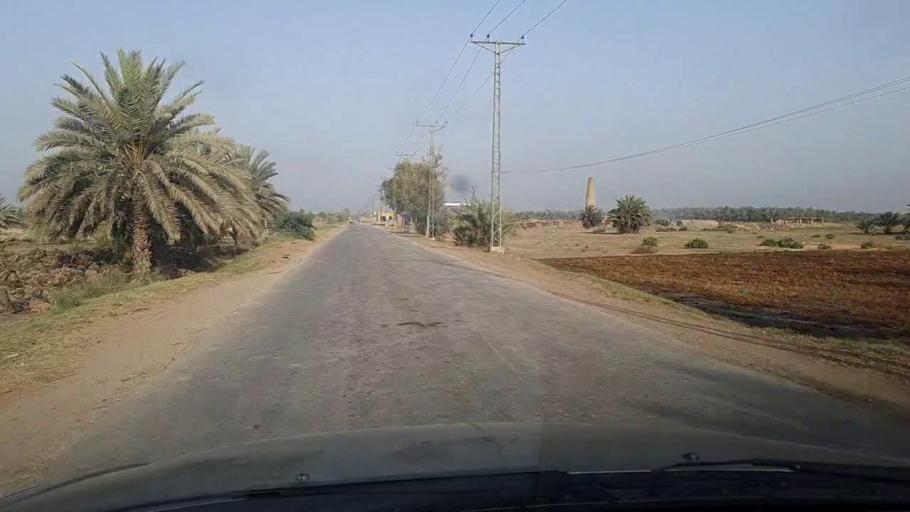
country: PK
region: Sindh
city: Pir jo Goth
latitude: 27.5688
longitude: 68.6367
